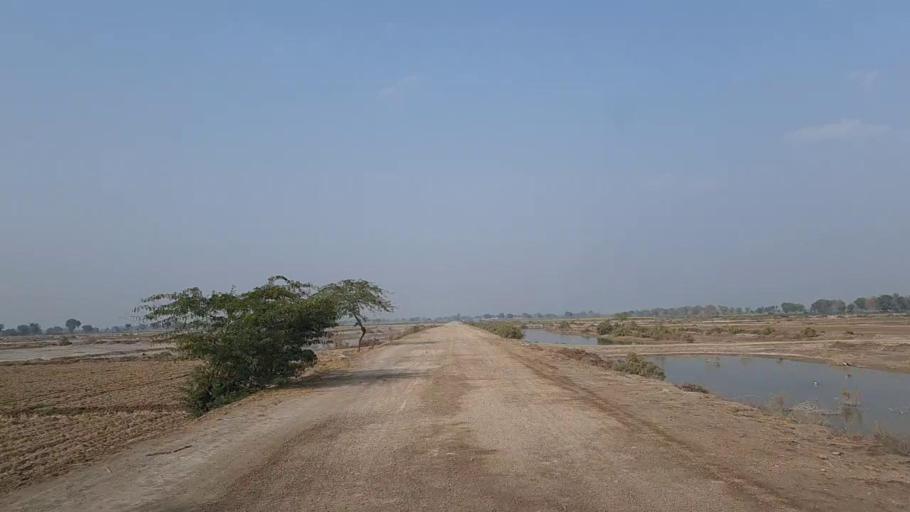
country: PK
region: Sindh
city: Nawabshah
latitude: 26.3403
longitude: 68.4738
